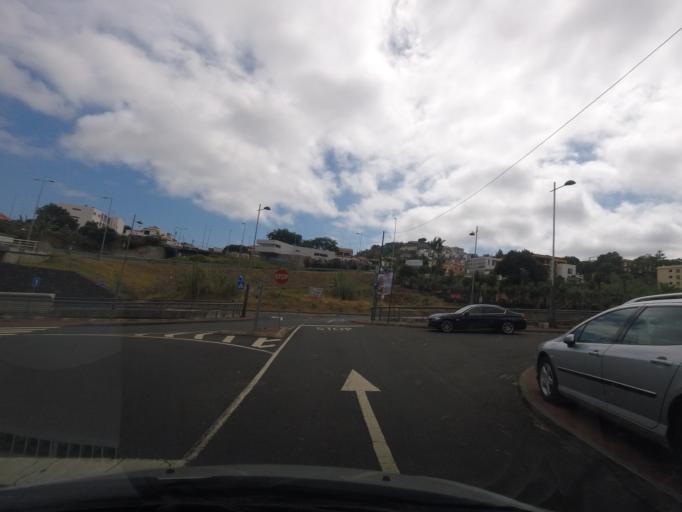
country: PT
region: Madeira
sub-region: Funchal
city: Nossa Senhora do Monte
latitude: 32.6629
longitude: -16.9328
